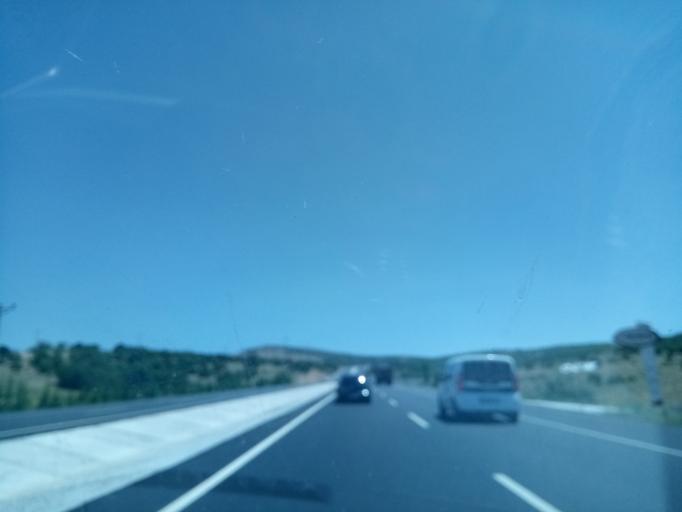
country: TR
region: Konya
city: Kiziloren
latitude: 37.7646
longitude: 32.2424
